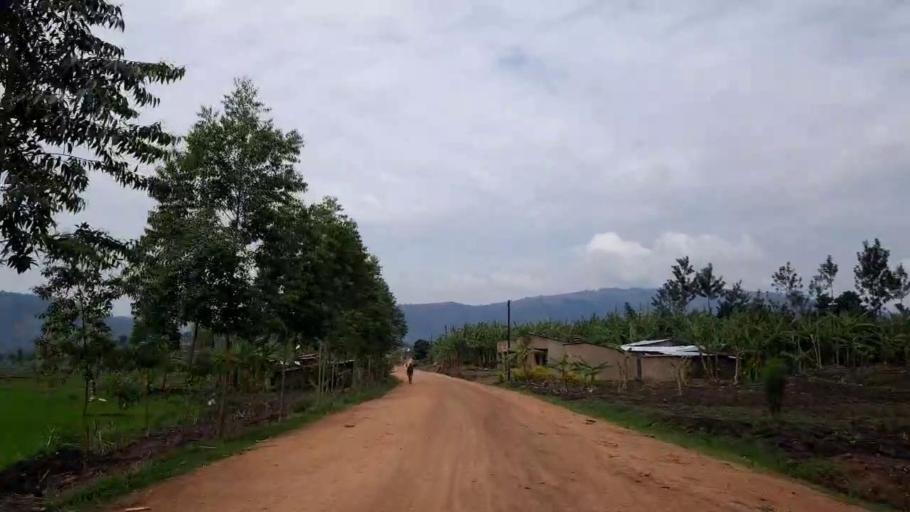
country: RW
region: Northern Province
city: Byumba
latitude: -1.4985
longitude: 30.2202
